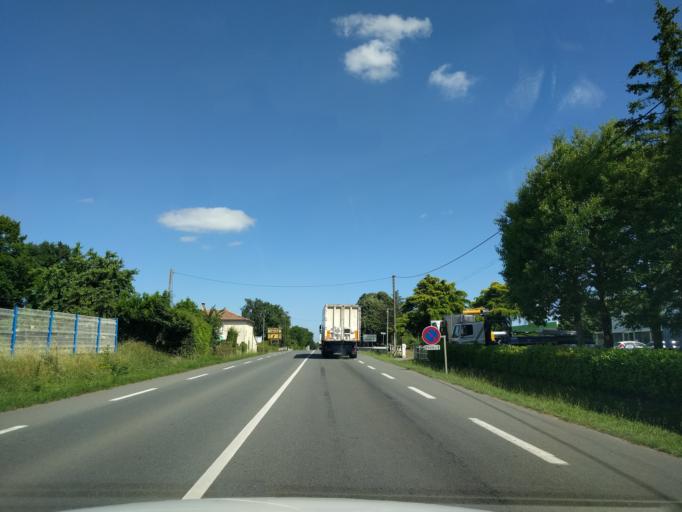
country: FR
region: Pays de la Loire
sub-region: Departement de la Vendee
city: Chantonnay
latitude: 46.7036
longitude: -1.0613
